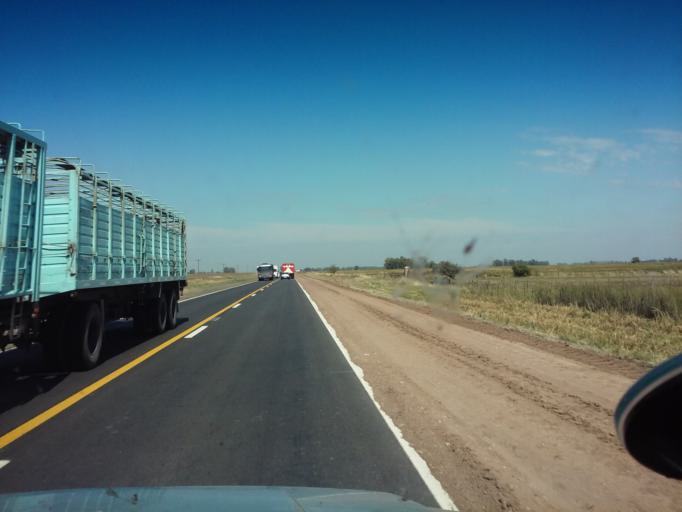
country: AR
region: Buenos Aires
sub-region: Partido de Nueve de Julio
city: Nueve de Julio
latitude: -35.3710
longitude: -60.7152
